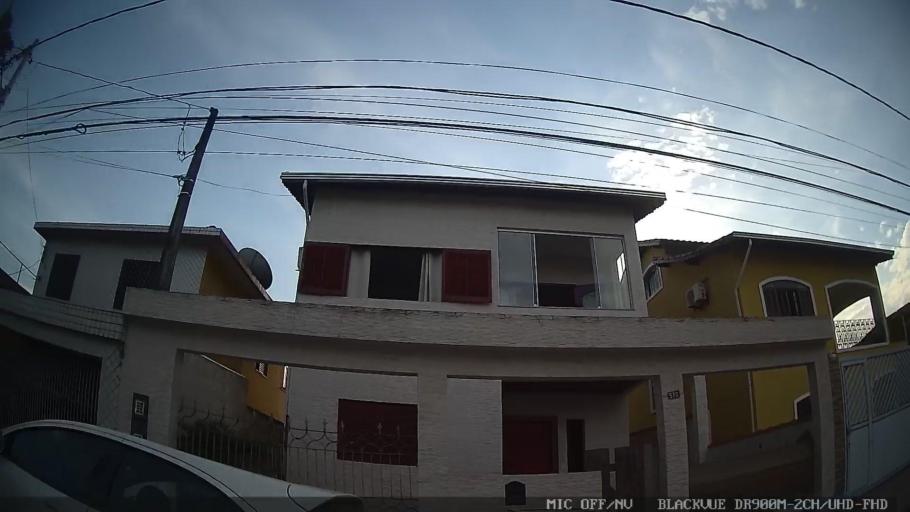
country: BR
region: Sao Paulo
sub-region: Cubatao
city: Cubatao
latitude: -23.8947
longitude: -46.4246
